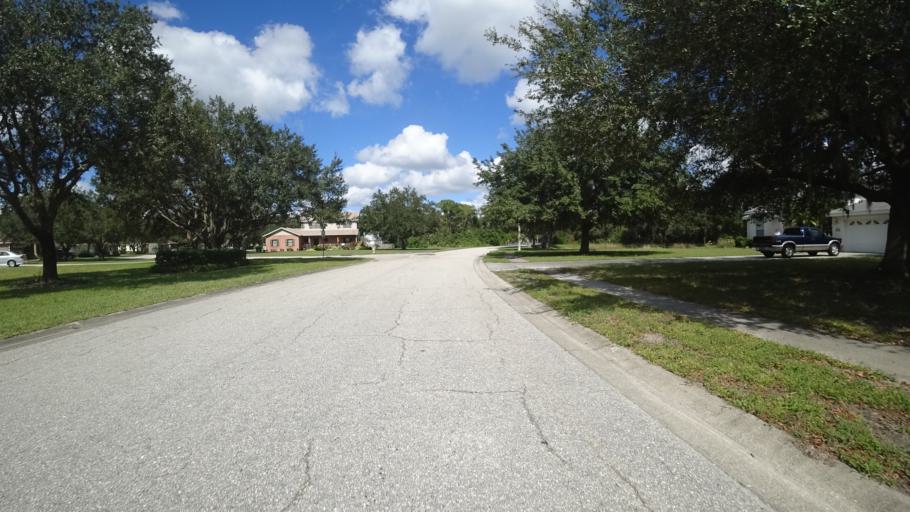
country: US
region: Florida
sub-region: Manatee County
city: Ellenton
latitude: 27.5047
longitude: -82.4022
